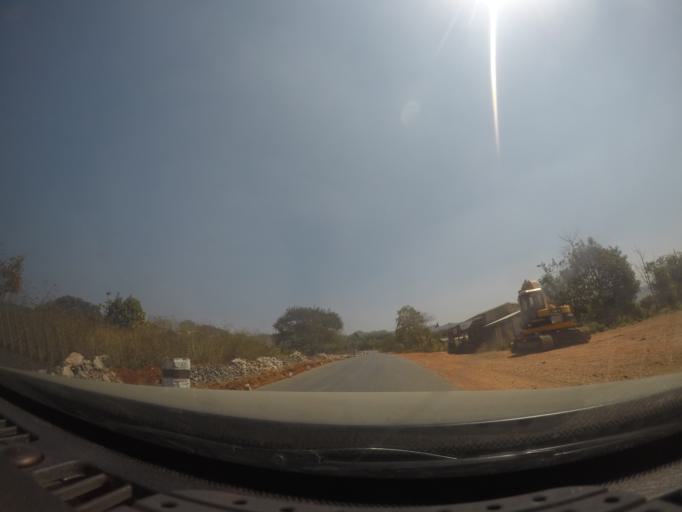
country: MM
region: Shan
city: Taunggyi
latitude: 20.8068
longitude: 97.2658
